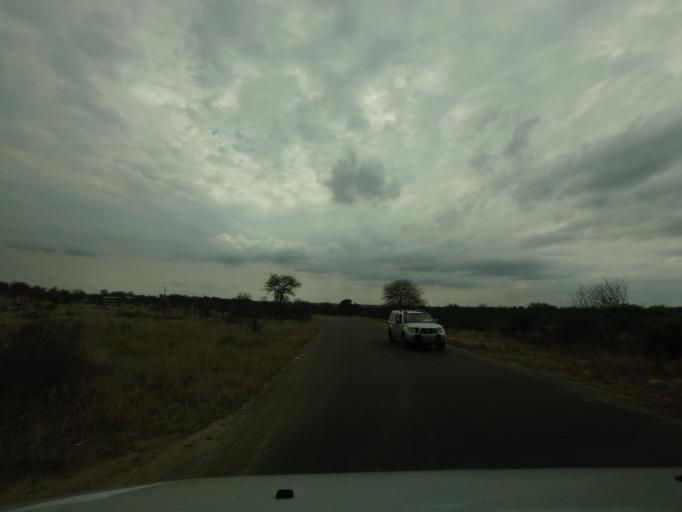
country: ZA
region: Limpopo
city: Thulamahashi
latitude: -24.4804
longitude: 31.3908
